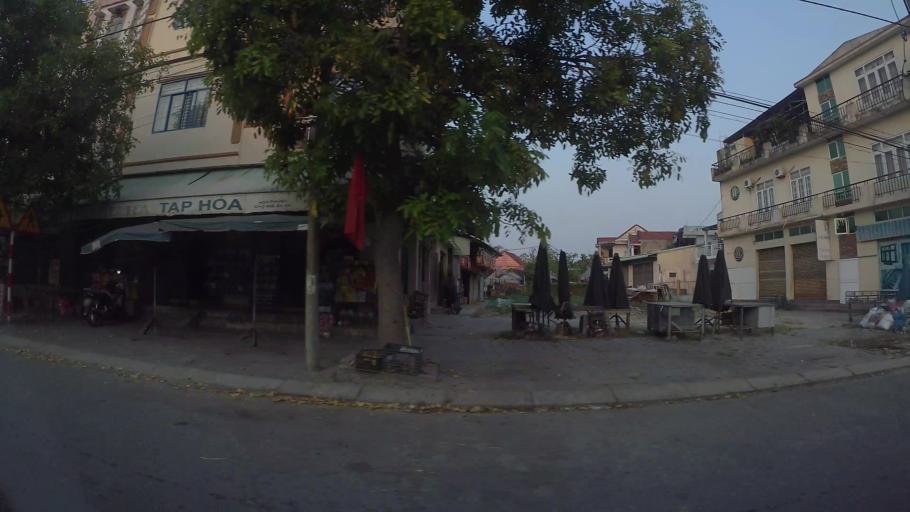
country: VN
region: Da Nang
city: Cam Le
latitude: 15.9497
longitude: 108.2194
